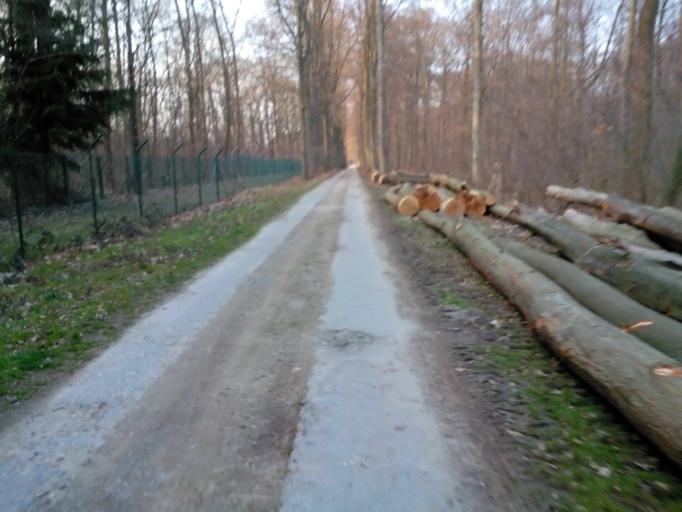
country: BE
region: Flanders
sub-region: Provincie Vlaams-Brabant
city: Oud-Heverlee
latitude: 50.8152
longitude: 4.6960
